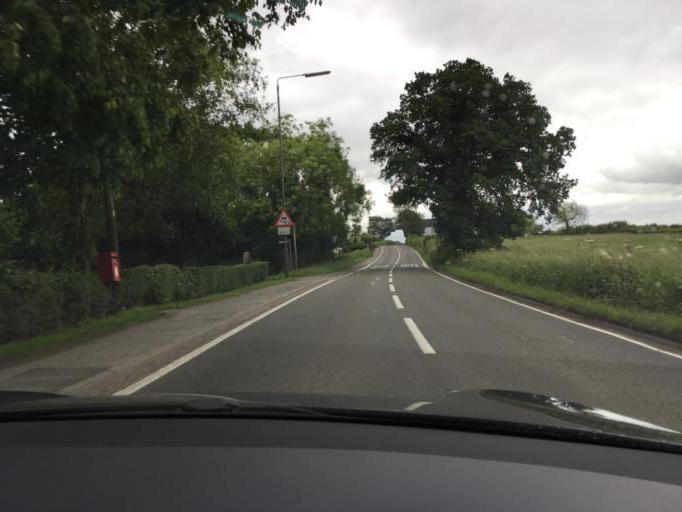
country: GB
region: England
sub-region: Derbyshire
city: Ashbourne
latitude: 53.0031
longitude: -1.7116
